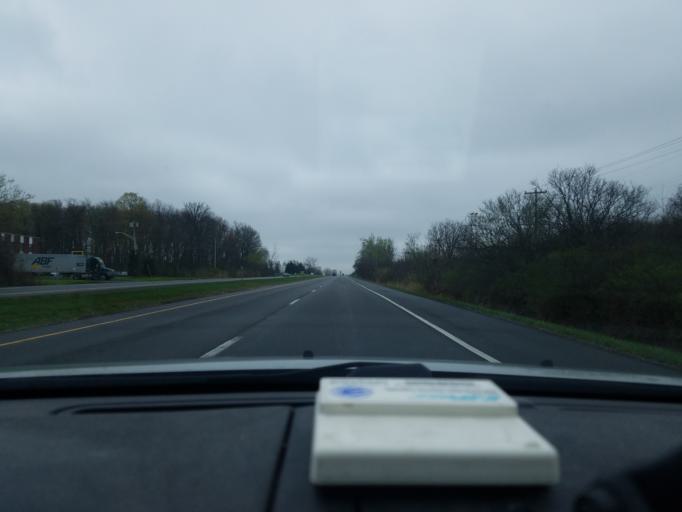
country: US
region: New York
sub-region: Onondaga County
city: East Syracuse
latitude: 43.1117
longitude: -76.0778
